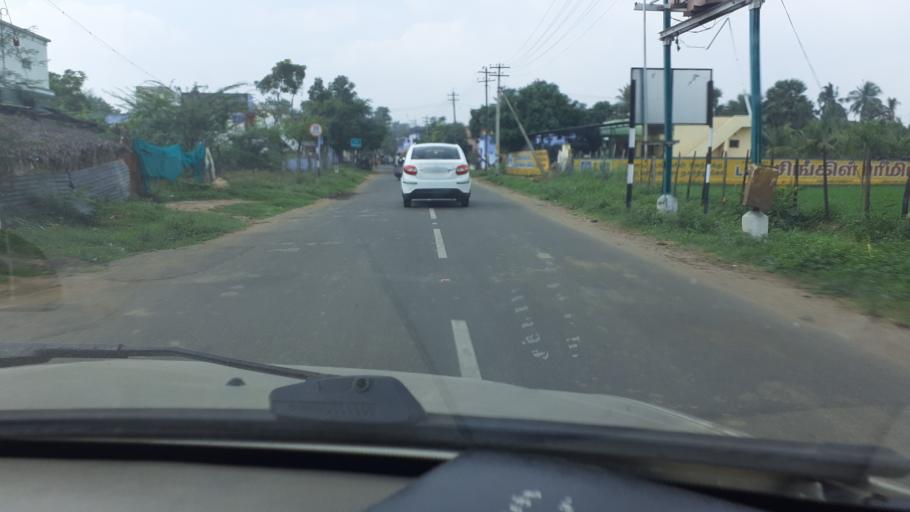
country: IN
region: Tamil Nadu
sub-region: Tirunelveli Kattabo
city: Viravanallur
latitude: 8.7194
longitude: 77.5475
